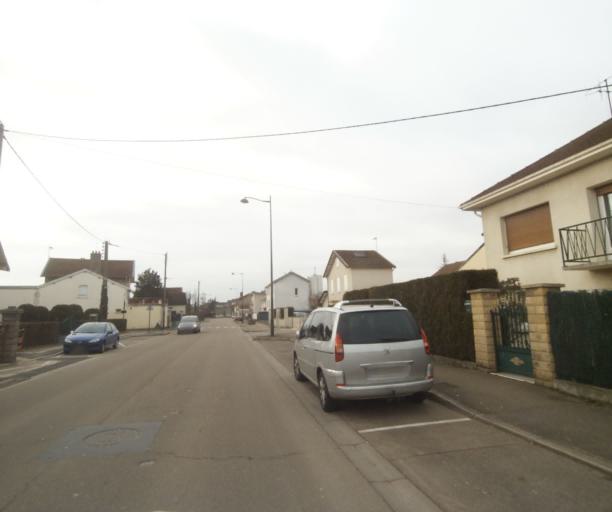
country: FR
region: Champagne-Ardenne
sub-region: Departement de la Haute-Marne
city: Bettancourt-la-Ferree
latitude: 48.6418
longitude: 4.9618
